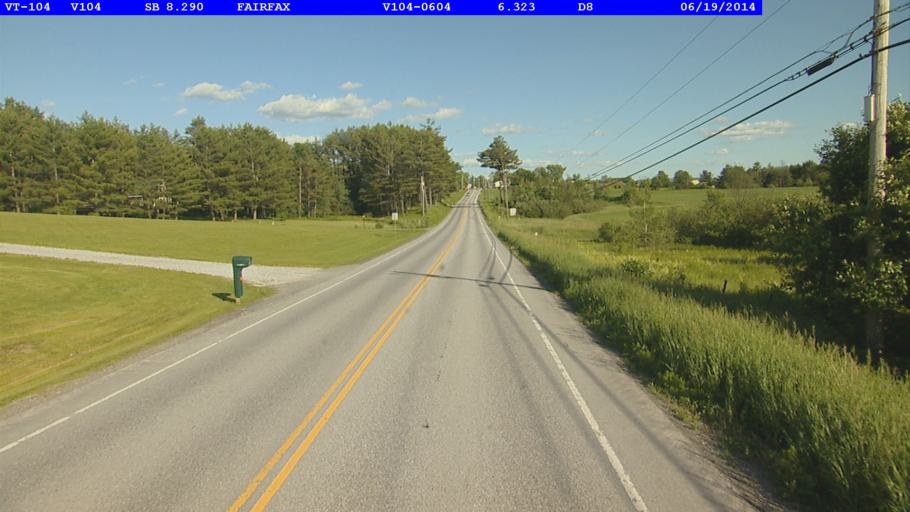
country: US
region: Vermont
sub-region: Chittenden County
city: Milton
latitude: 44.6778
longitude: -73.0237
